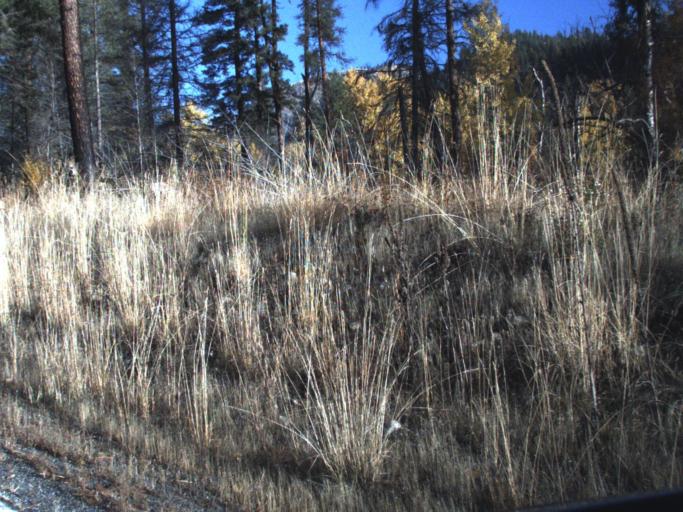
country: US
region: Washington
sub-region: Ferry County
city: Republic
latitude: 48.2867
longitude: -118.7267
